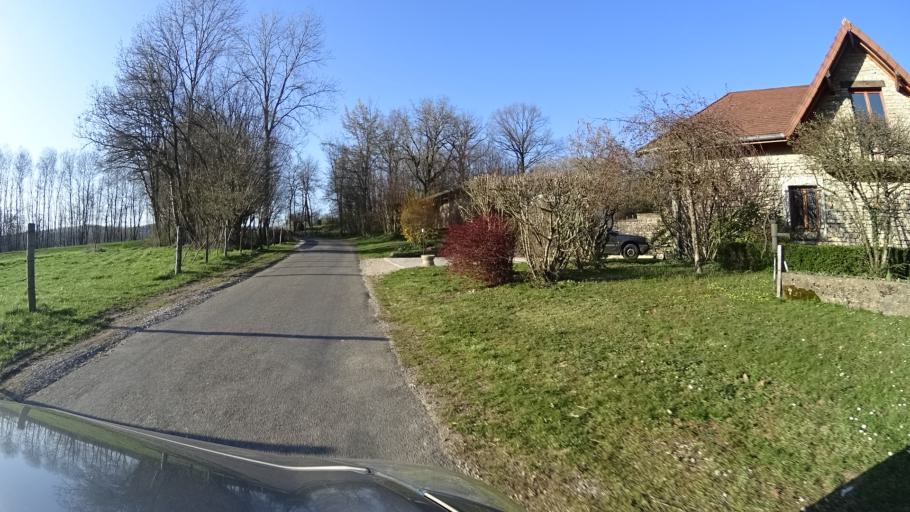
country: FR
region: Franche-Comte
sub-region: Departement du Doubs
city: Morre
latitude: 47.1902
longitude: 6.0551
